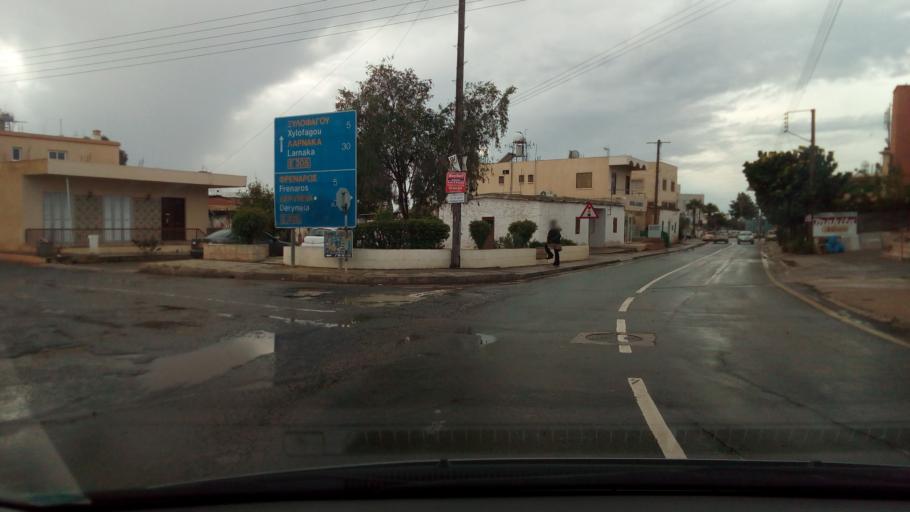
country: CY
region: Ammochostos
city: Liopetri
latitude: 35.0101
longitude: 33.8947
